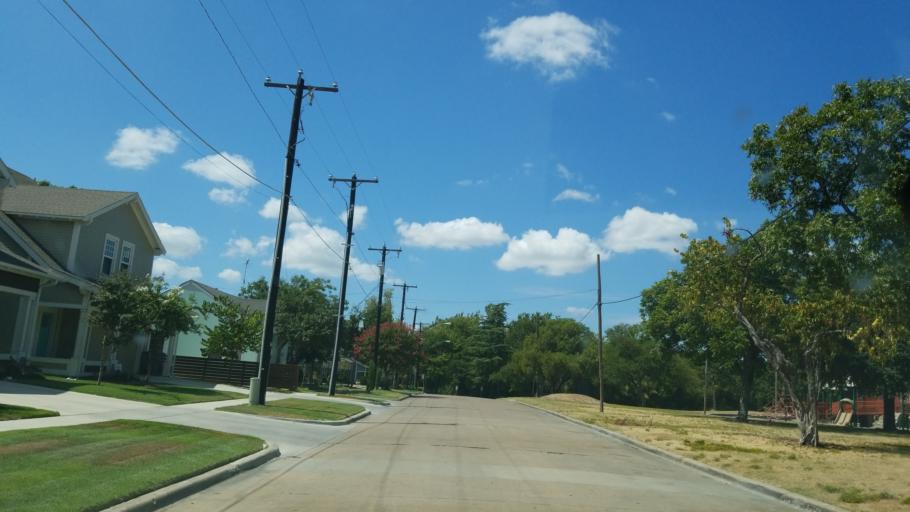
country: US
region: Texas
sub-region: Dallas County
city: Dallas
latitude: 32.7545
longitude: -96.8317
